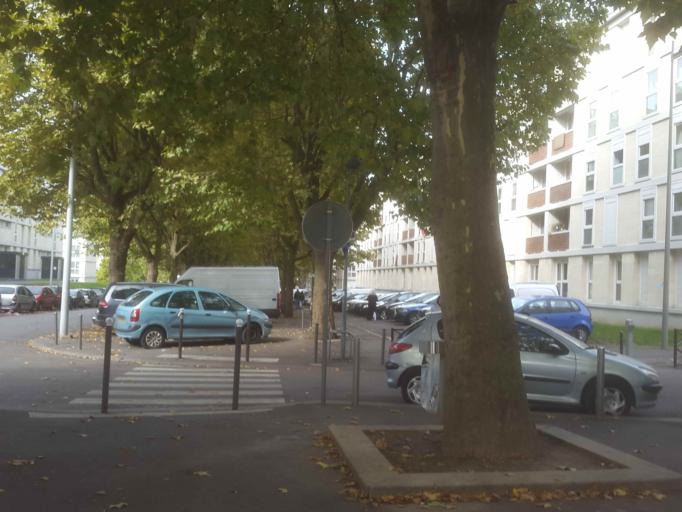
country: FR
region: Ile-de-France
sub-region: Departement du Val-d'Oise
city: Garges-les-Gonesse
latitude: 48.9768
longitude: 2.3885
